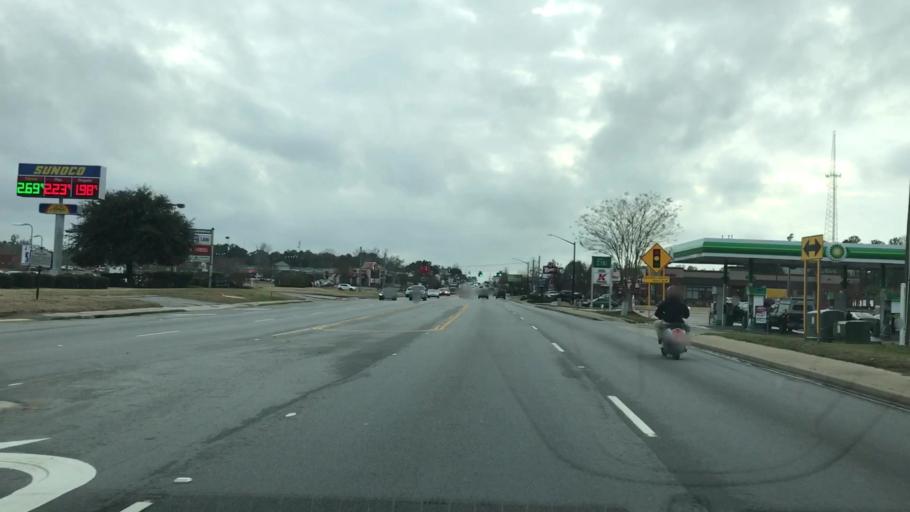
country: US
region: South Carolina
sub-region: Berkeley County
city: Moncks Corner
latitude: 33.2109
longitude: -79.9805
